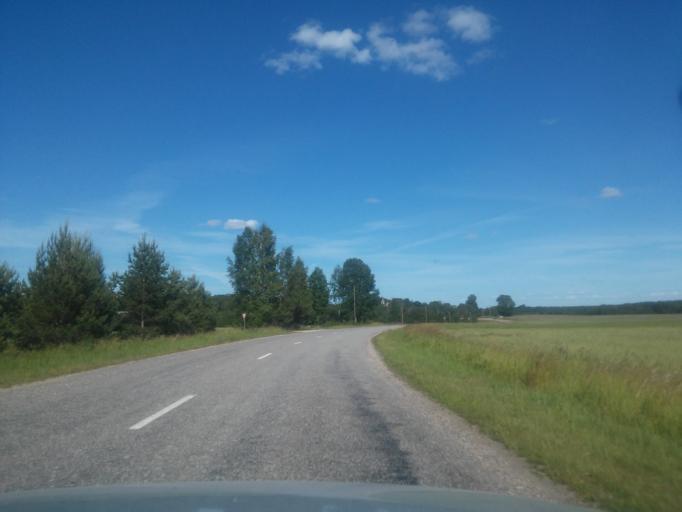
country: LV
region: Skrunda
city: Skrunda
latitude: 56.6233
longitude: 21.9713
